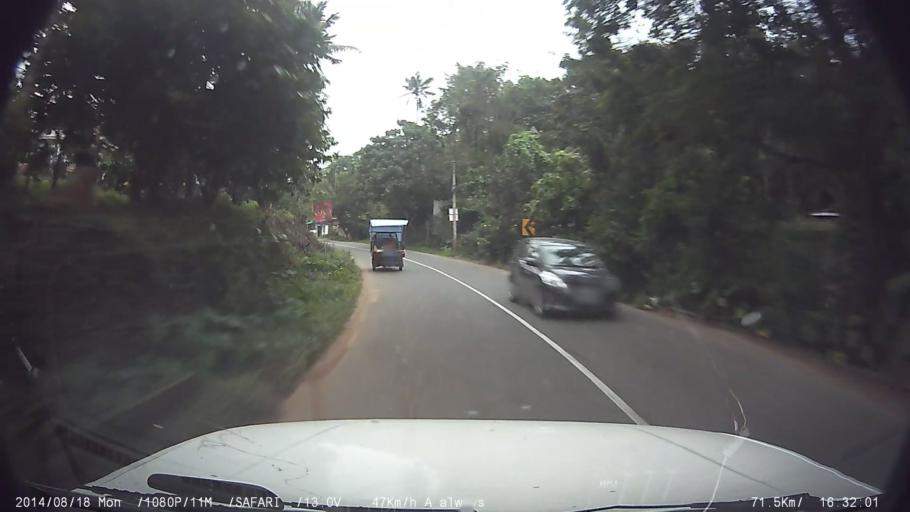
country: IN
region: Kerala
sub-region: Kottayam
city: Palackattumala
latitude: 9.8005
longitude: 76.5746
